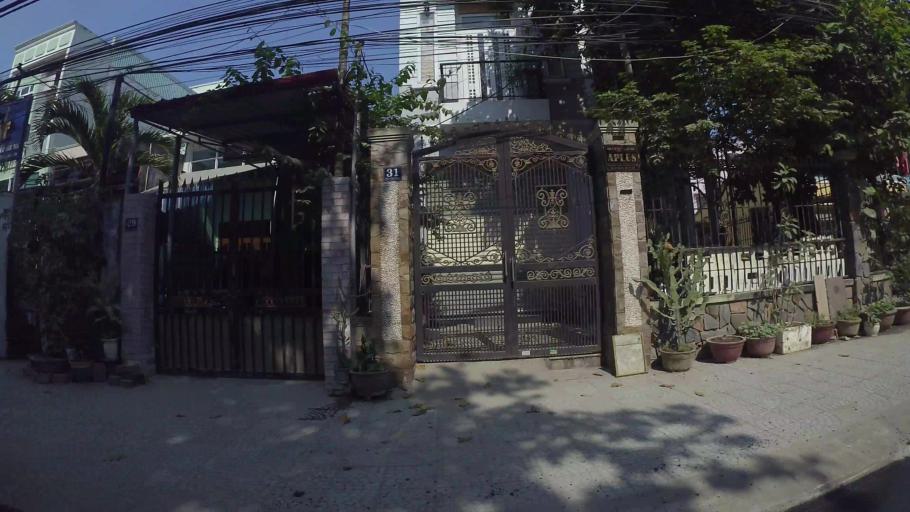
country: VN
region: Da Nang
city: Ngu Hanh Son
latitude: 16.0396
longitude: 108.2479
